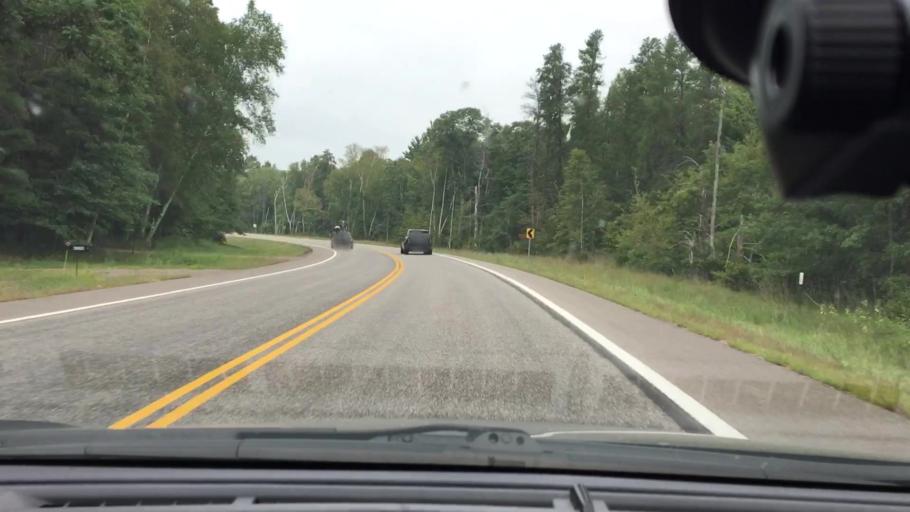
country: US
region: Minnesota
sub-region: Crow Wing County
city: Cross Lake
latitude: 46.6652
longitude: -94.0389
